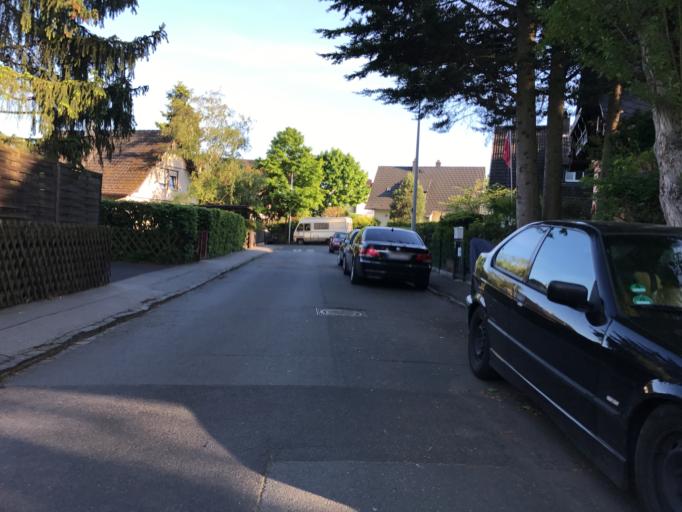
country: DE
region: Rheinland-Pfalz
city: Mainz
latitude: 50.0165
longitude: 8.2279
